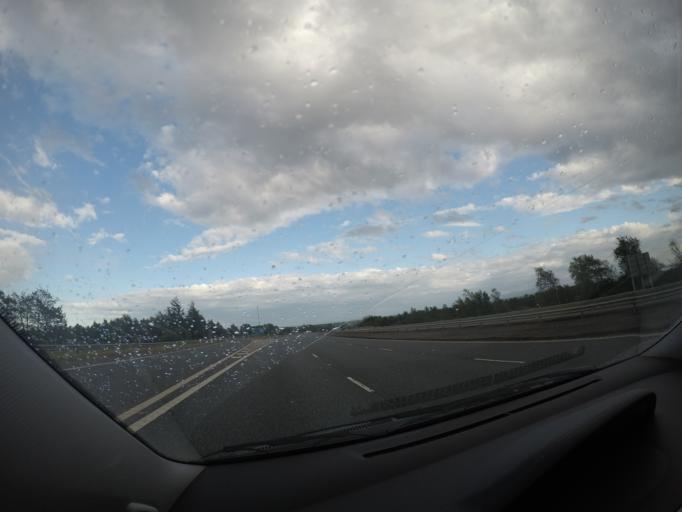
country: GB
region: Scotland
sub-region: Dumfries and Galloway
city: Gretna
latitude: 55.0029
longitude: -3.0615
